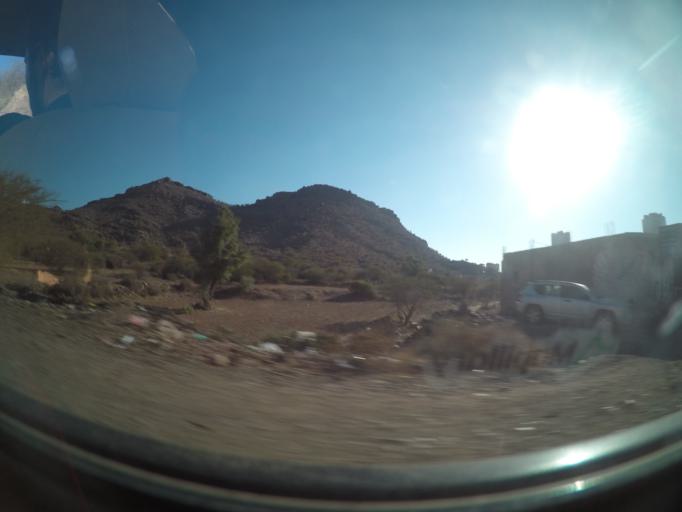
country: YE
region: Ad Dali'
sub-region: Ad Dhale'e
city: Dhalie
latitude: 13.6736
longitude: 44.7629
